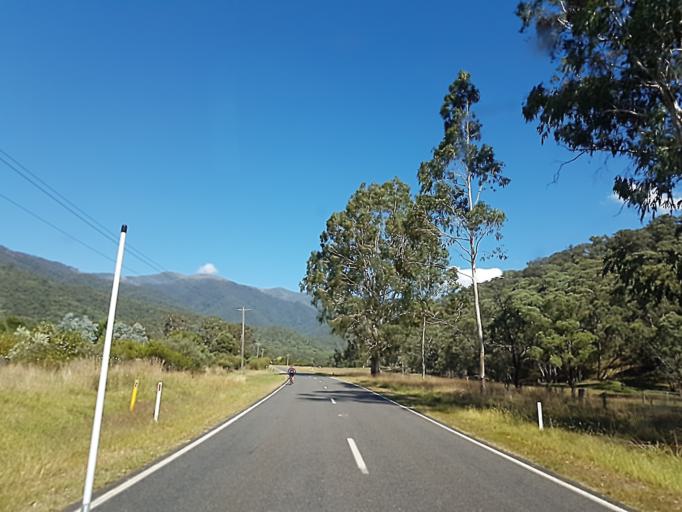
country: AU
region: Victoria
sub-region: Alpine
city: Mount Beauty
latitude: -36.8328
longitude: 147.0741
